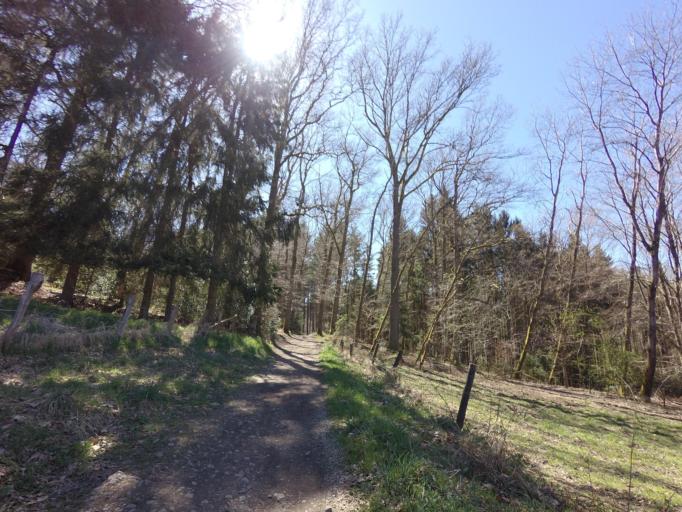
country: BE
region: Wallonia
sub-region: Province de Liege
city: Trois-Ponts
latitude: 50.4052
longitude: 5.8678
